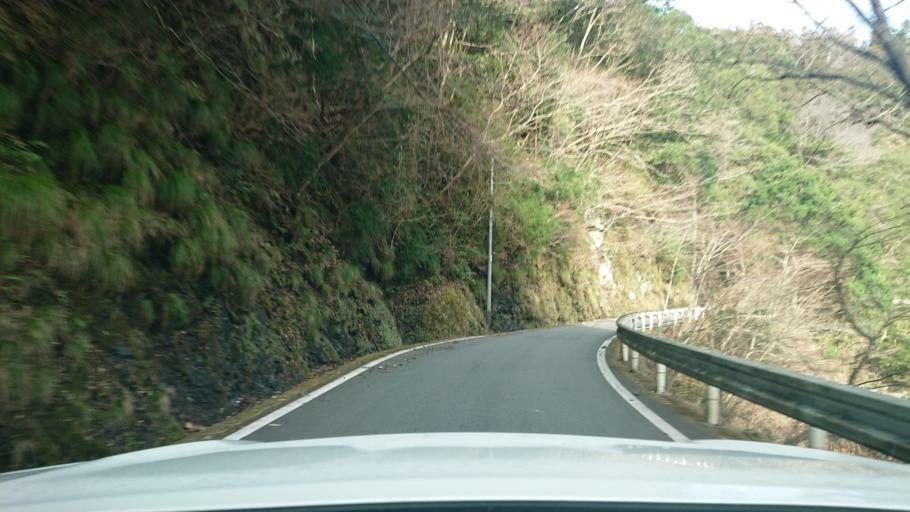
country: JP
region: Tokushima
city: Ishii
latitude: 33.9000
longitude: 134.3956
